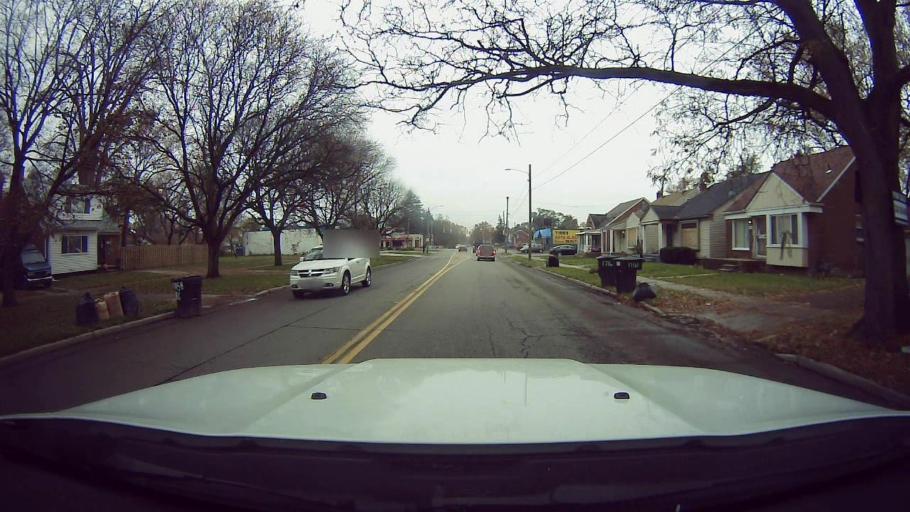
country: US
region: Michigan
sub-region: Oakland County
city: Southfield
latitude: 42.4162
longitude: -83.2383
